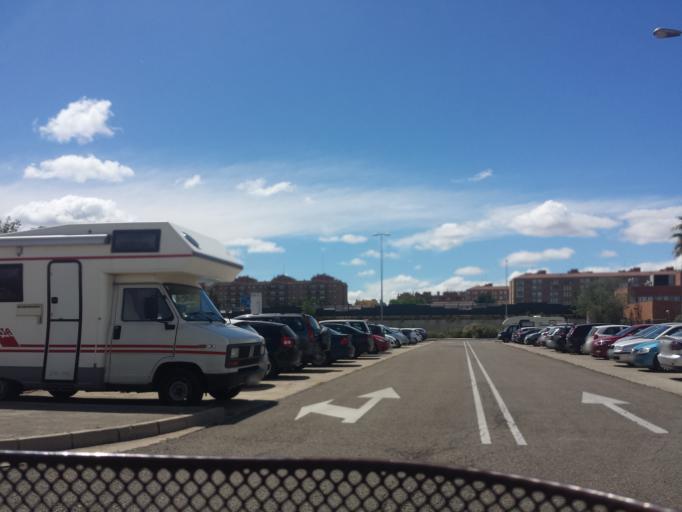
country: ES
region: Aragon
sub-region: Provincia de Zaragoza
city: Almozara
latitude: 41.6818
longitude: -0.8875
